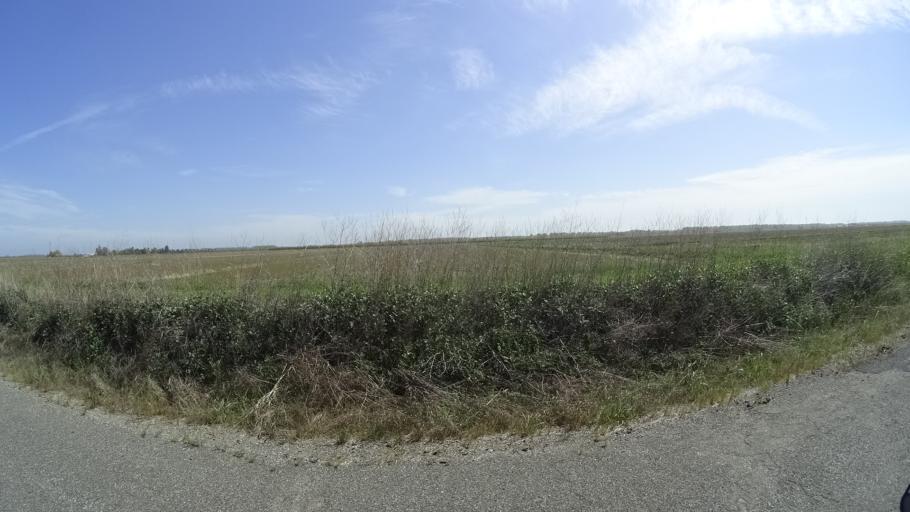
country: US
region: California
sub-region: Glenn County
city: Hamilton City
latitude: 39.5983
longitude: -122.0276
